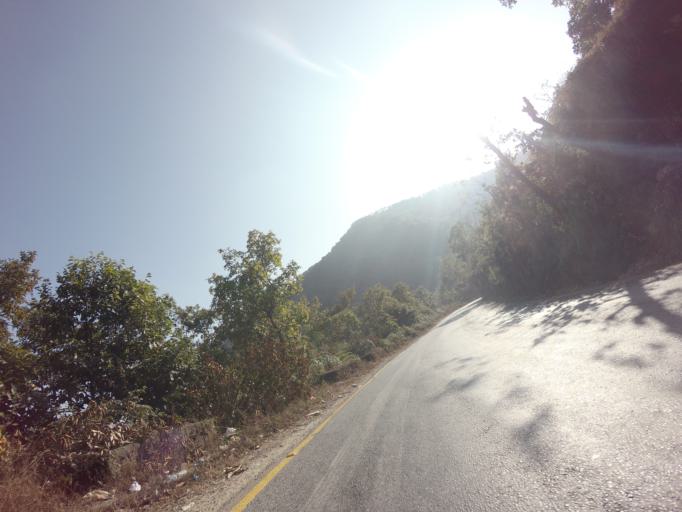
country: NP
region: Western Region
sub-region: Gandaki Zone
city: Pokhara
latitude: 28.1886
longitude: 83.9038
